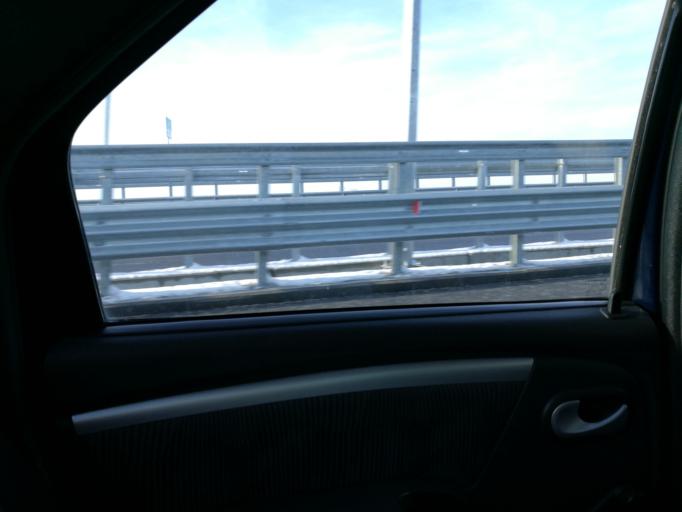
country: RO
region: Ilfov
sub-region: Voluntari City
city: Voluntari
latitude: 44.4833
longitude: 26.1393
